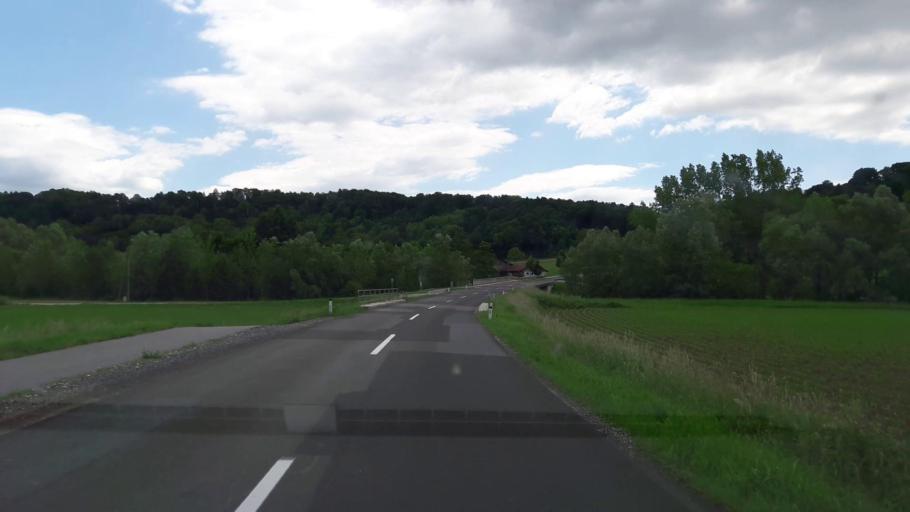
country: AT
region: Styria
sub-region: Politischer Bezirk Hartberg-Fuerstenfeld
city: Soechau
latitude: 47.0637
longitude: 16.0081
